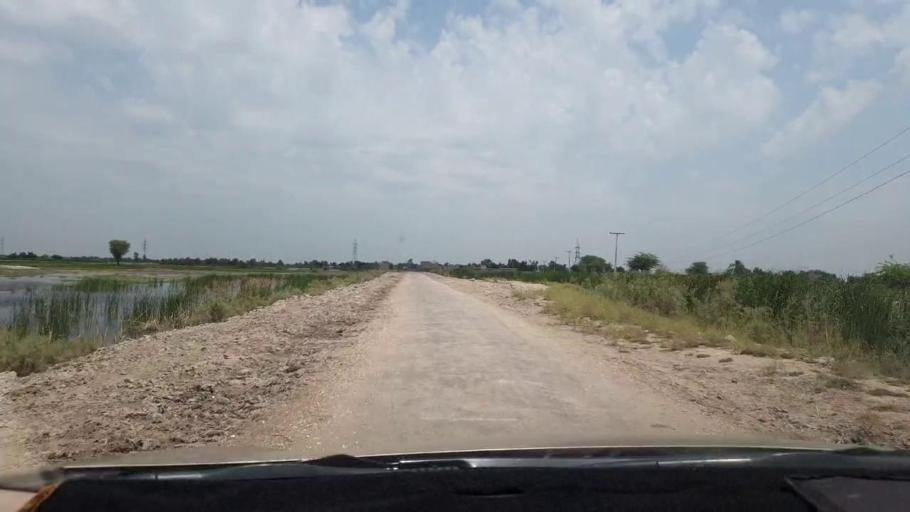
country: PK
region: Sindh
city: Naudero
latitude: 27.7228
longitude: 68.3318
